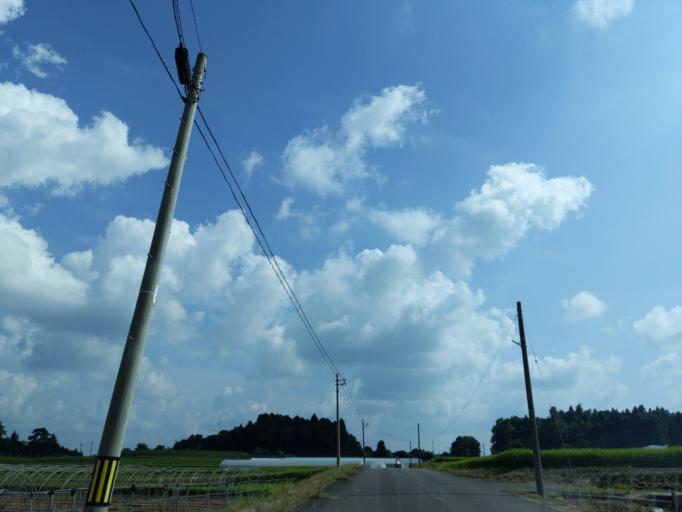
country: JP
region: Fukushima
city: Sukagawa
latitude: 37.3399
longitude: 140.3257
